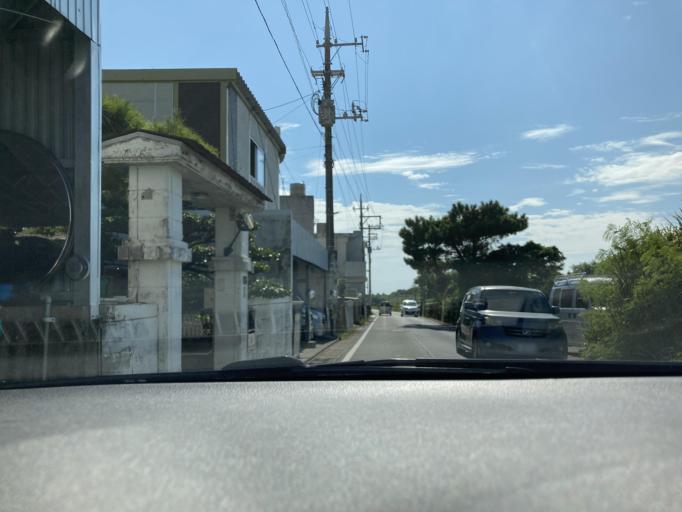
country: JP
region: Okinawa
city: Chatan
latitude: 26.3669
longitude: 127.7417
